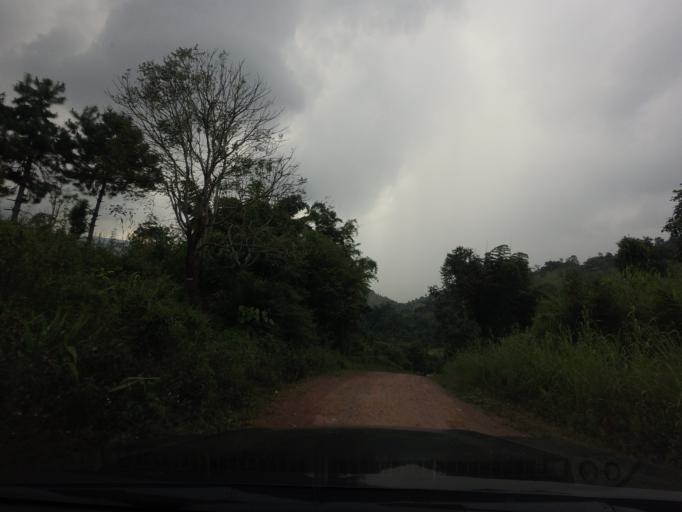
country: TH
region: Nan
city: Bo Kluea
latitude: 19.3516
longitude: 101.1737
